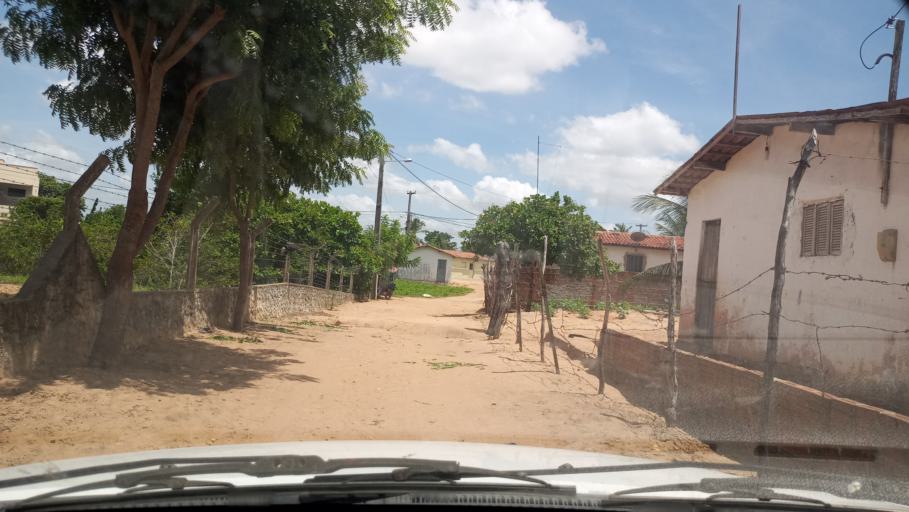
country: BR
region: Rio Grande do Norte
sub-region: Brejinho
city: Brejinho
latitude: -6.2650
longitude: -35.3738
